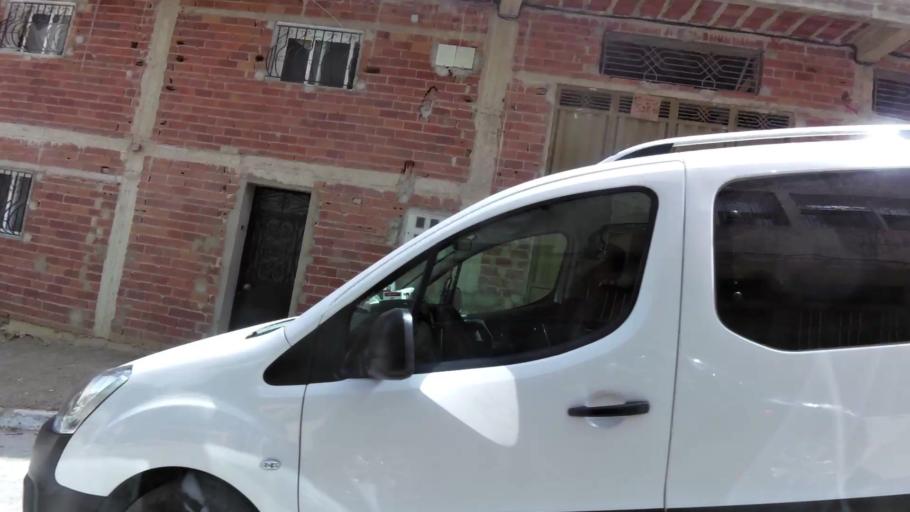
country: MA
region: Tanger-Tetouan
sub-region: Tanger-Assilah
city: Tangier
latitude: 35.7472
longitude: -5.8311
